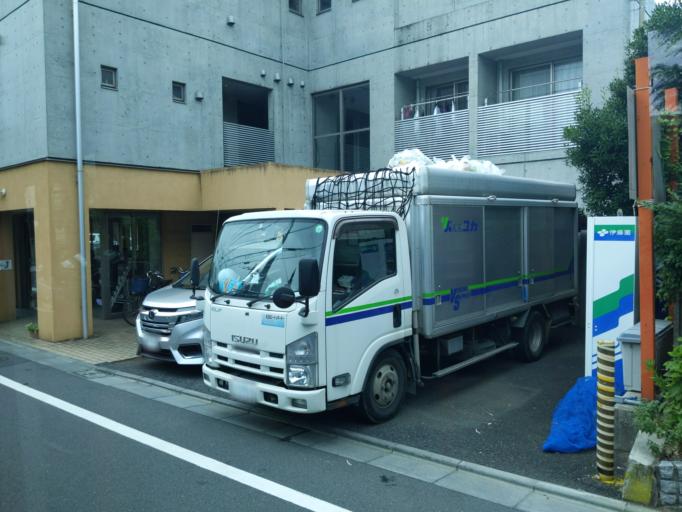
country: JP
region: Saitama
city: Wako
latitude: 35.7802
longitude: 139.6471
